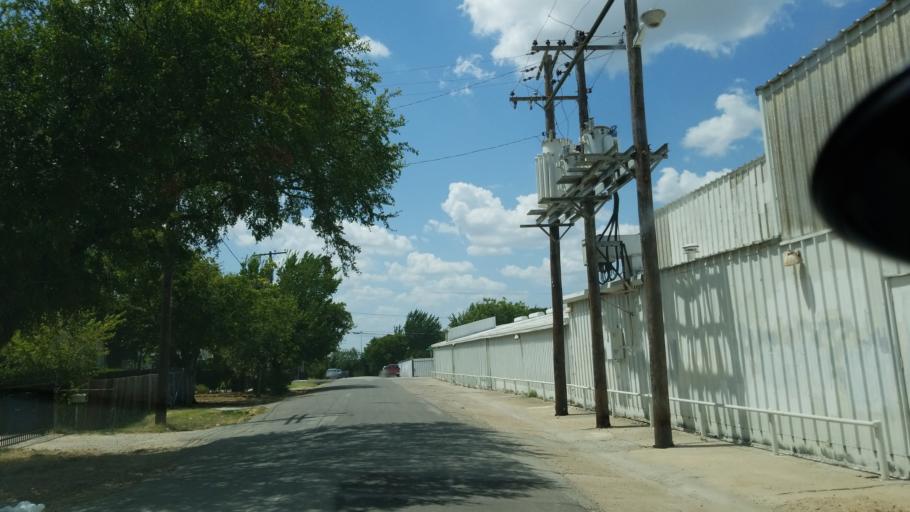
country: US
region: Texas
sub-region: Dallas County
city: Cockrell Hill
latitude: 32.7440
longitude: -96.9092
